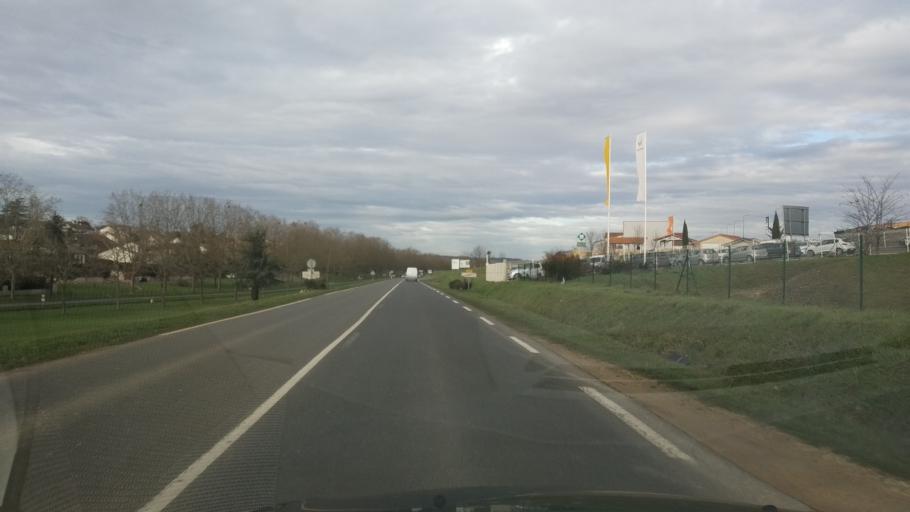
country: FR
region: Poitou-Charentes
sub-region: Departement de la Vienne
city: Saint-Georges-les-Baillargeaux
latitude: 46.6706
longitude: 0.4048
